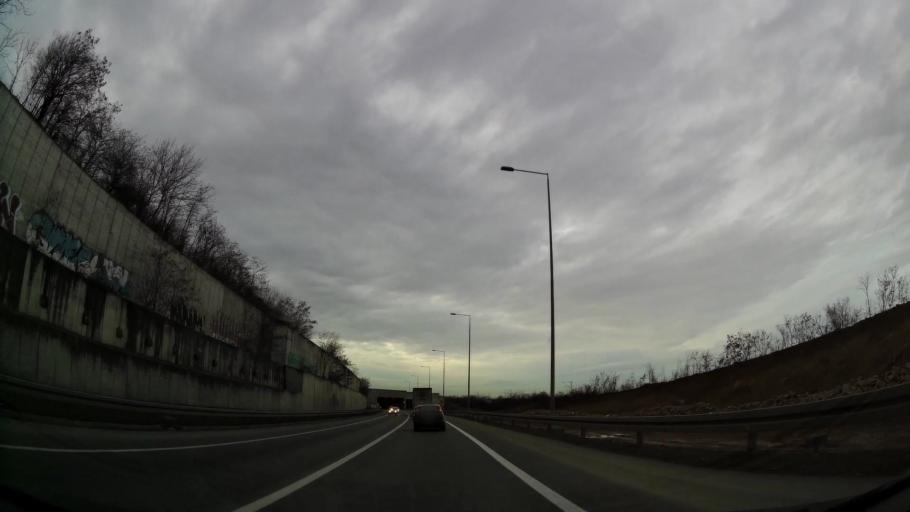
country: RS
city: Ostruznica
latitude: 44.7265
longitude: 20.3538
